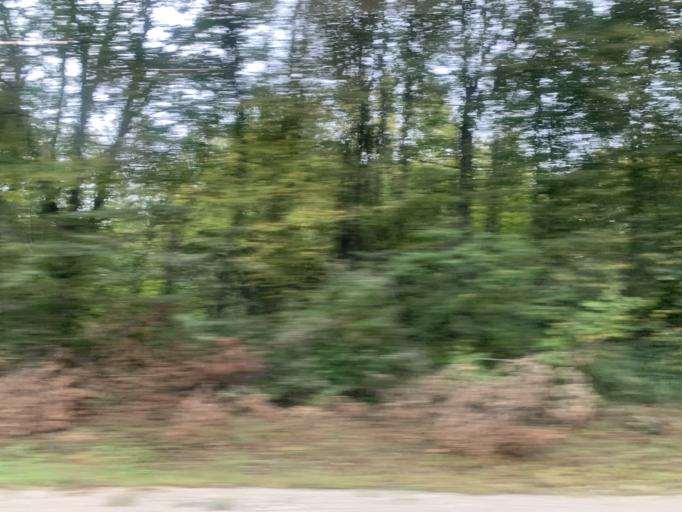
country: DE
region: Bavaria
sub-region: Upper Bavaria
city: Oberschleissheim
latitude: 48.2401
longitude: 11.5488
